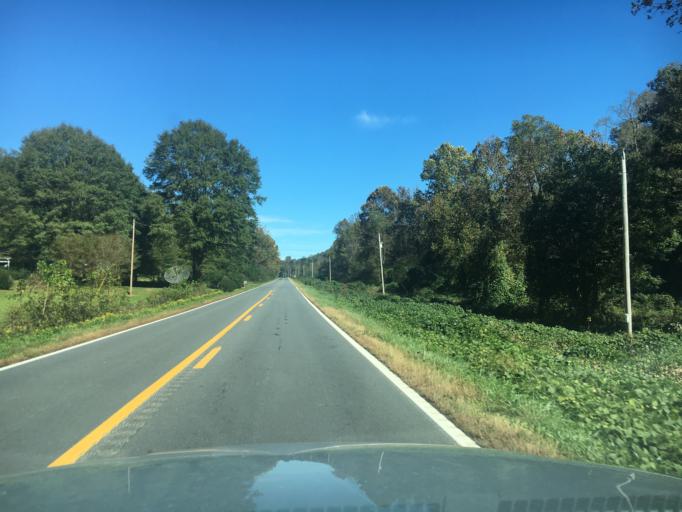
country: US
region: North Carolina
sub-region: Rutherford County
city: Spindale
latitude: 35.5433
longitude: -81.8564
